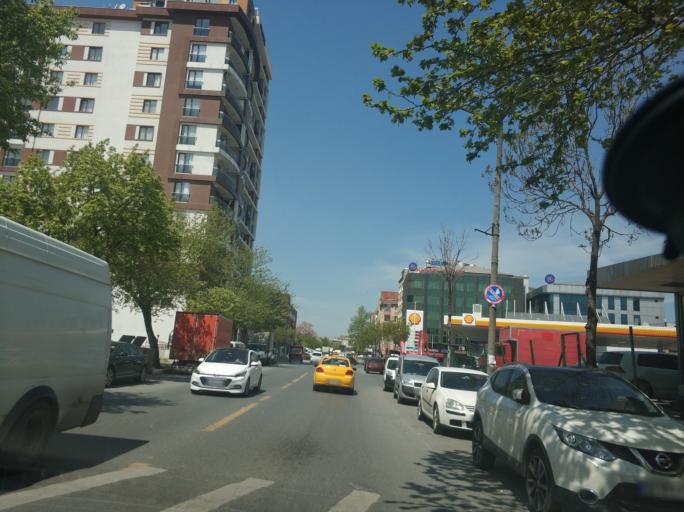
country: TR
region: Istanbul
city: Bagcilar
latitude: 41.0517
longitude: 28.8583
